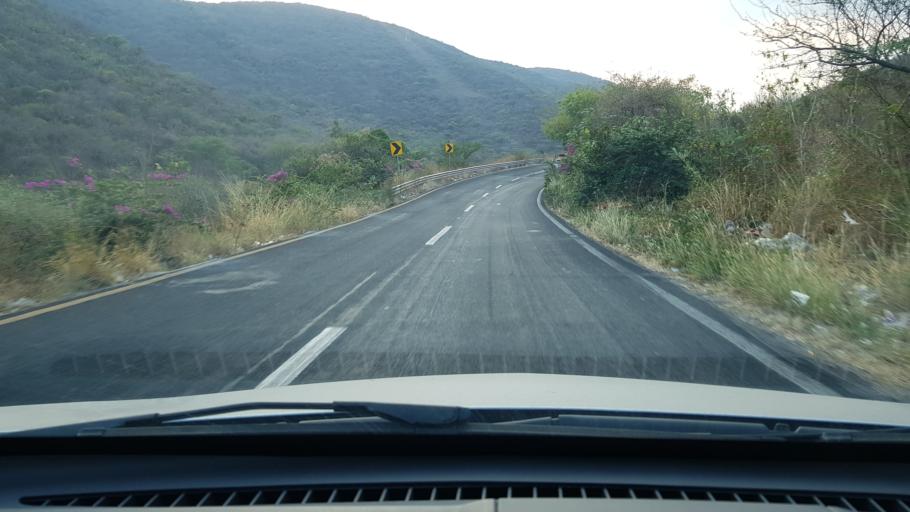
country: MX
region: Morelos
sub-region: Jiutepec
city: Independencia
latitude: 18.8565
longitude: -99.1132
